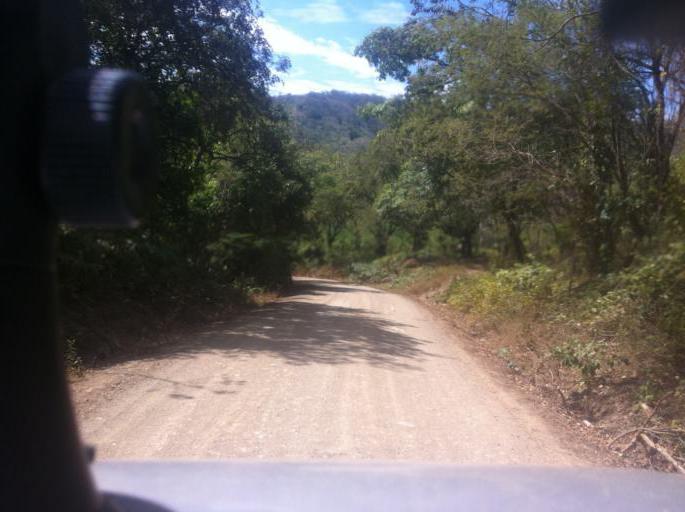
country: NI
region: Rivas
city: Tola
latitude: 11.5605
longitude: -86.0318
